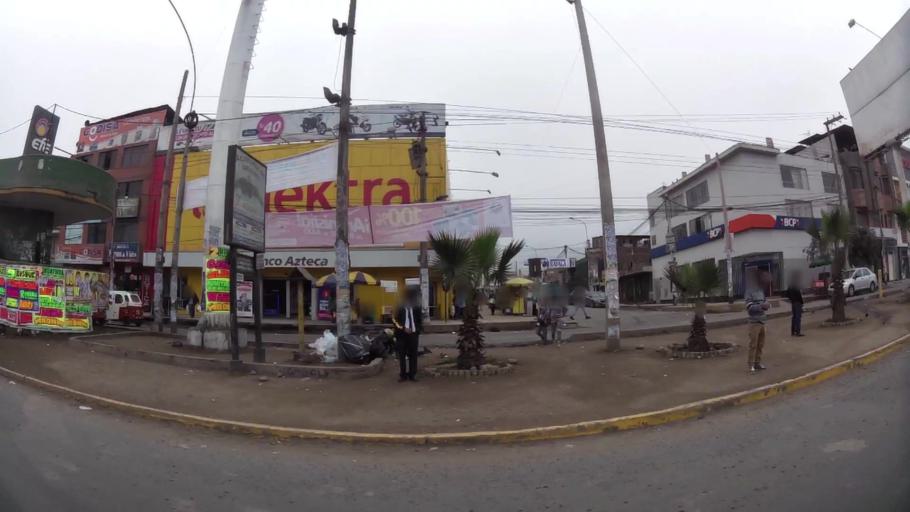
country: PE
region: Lima
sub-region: Lima
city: Surco
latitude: -12.1669
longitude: -76.9517
